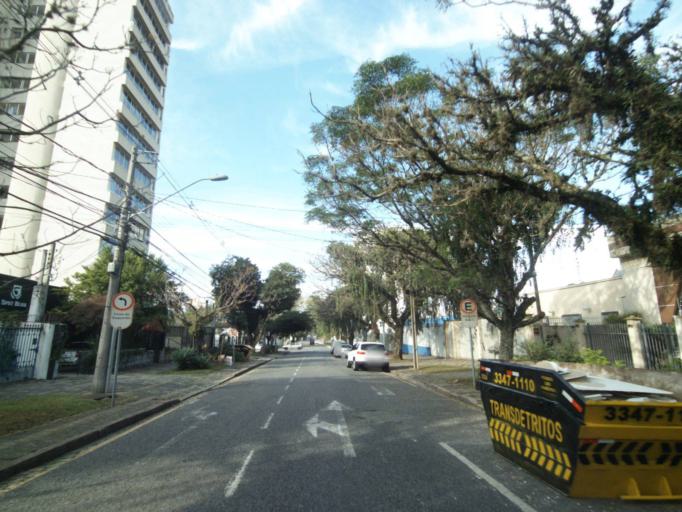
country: BR
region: Parana
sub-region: Curitiba
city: Curitiba
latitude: -25.4306
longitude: -49.2845
